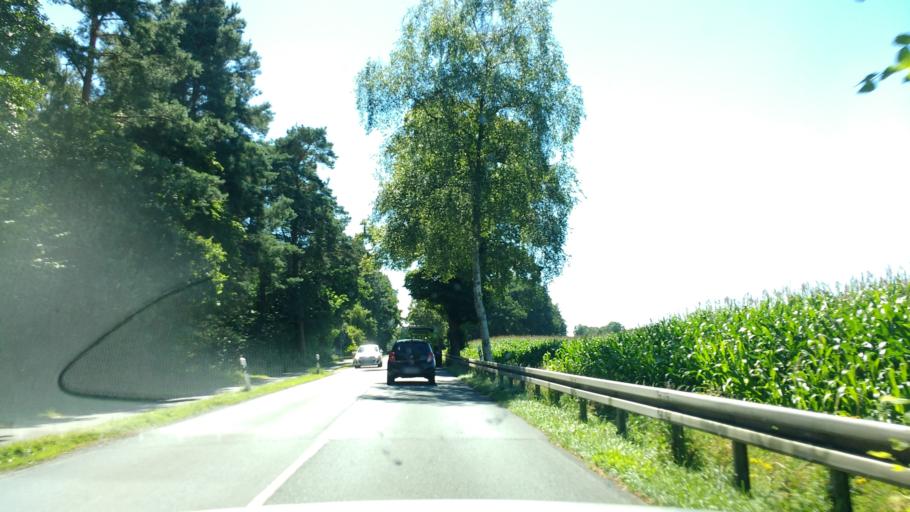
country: DE
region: North Rhine-Westphalia
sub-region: Regierungsbezirk Arnsberg
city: Lippstadt
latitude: 51.7018
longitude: 8.4169
